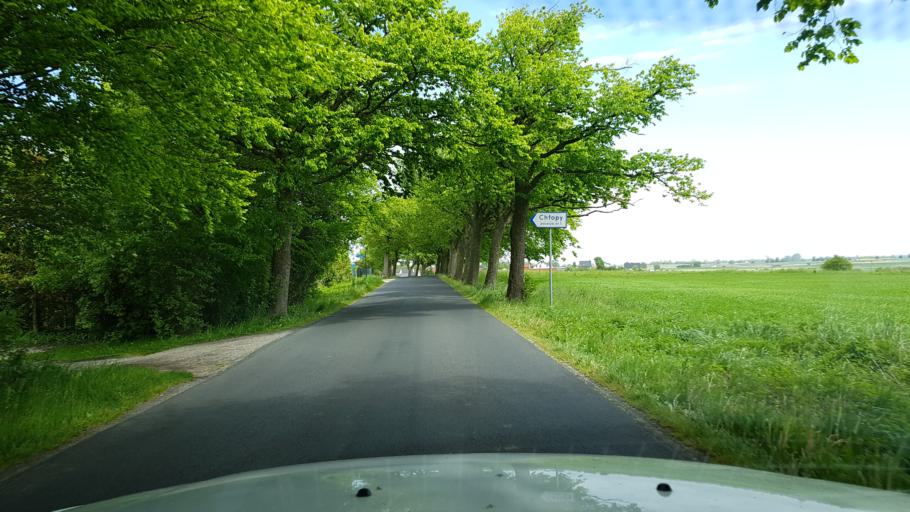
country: PL
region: West Pomeranian Voivodeship
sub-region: Powiat koszalinski
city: Mielno
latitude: 54.2447
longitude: 16.0031
